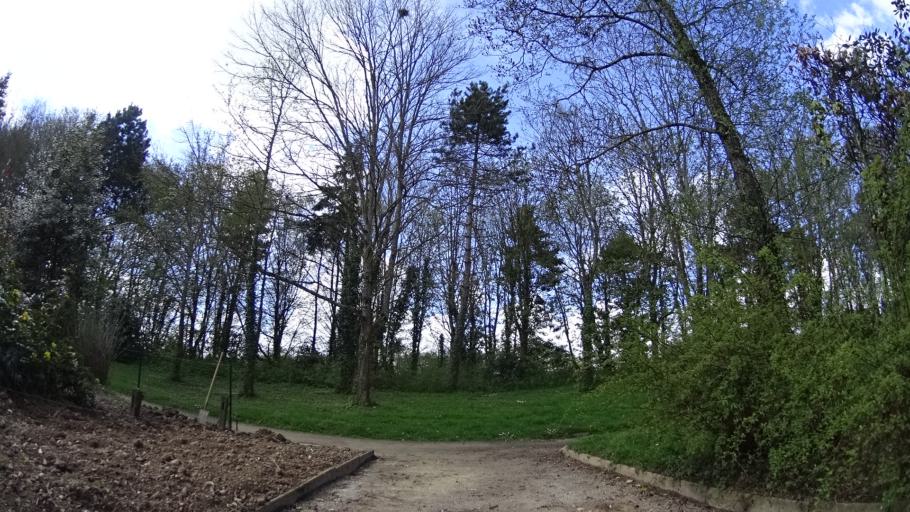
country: FR
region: Brittany
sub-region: Departement d'Ille-et-Vilaine
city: Rennes
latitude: 48.1309
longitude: -1.6656
